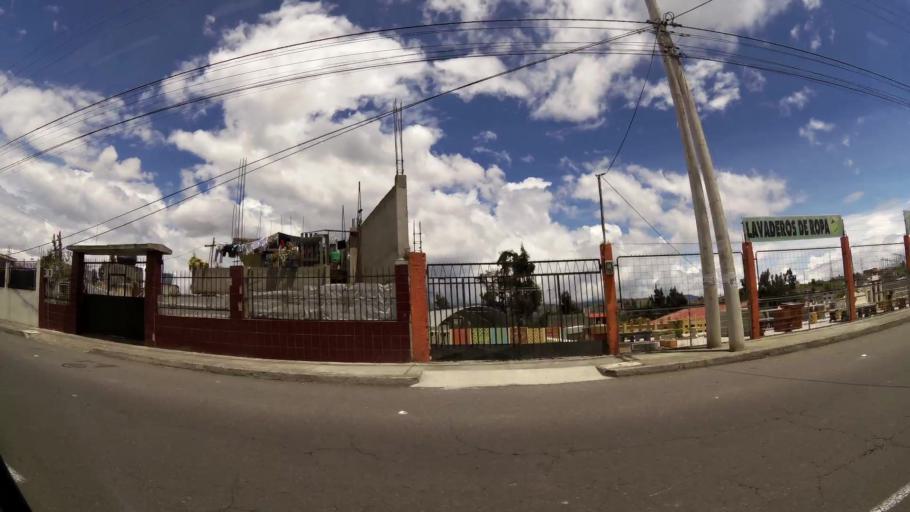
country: EC
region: Tungurahua
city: Ambato
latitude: -1.2935
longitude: -78.6038
